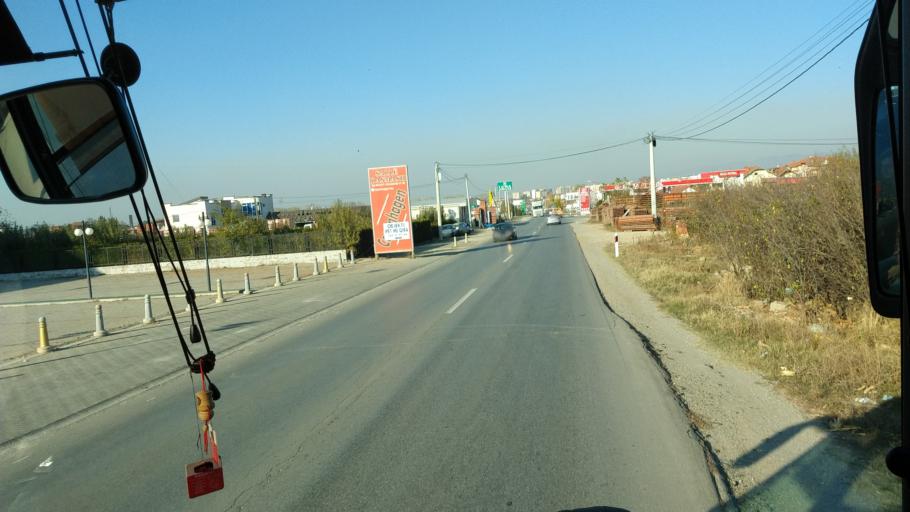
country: XK
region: Pristina
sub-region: Lipjan
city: Lipljan
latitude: 42.5053
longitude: 21.1106
